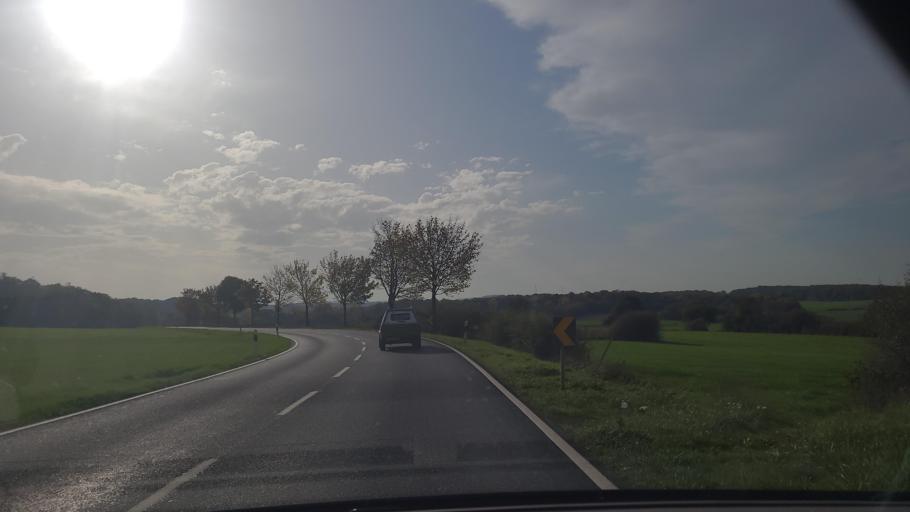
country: LU
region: Luxembourg
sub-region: Canton de Capellen
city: Kehlen
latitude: 49.6569
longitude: 6.0345
